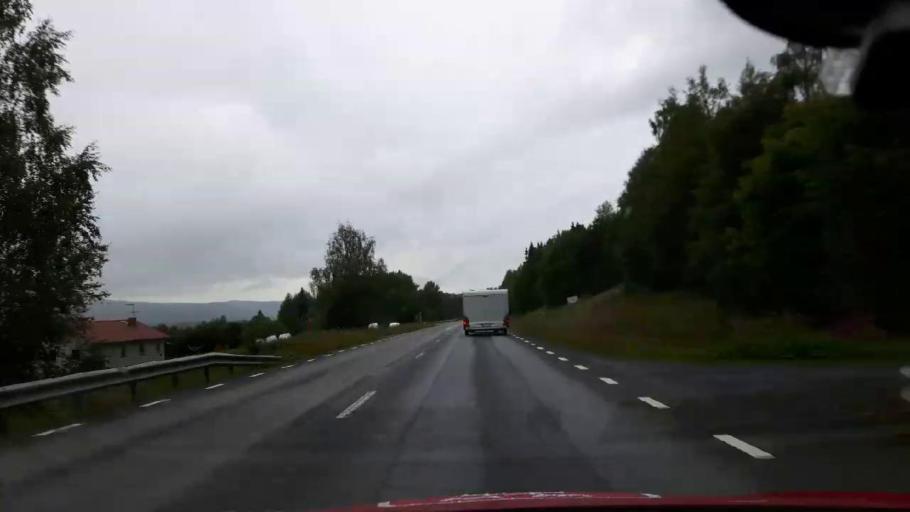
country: SE
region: Jaemtland
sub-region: Are Kommun
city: Jarpen
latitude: 63.3107
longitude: 13.6656
